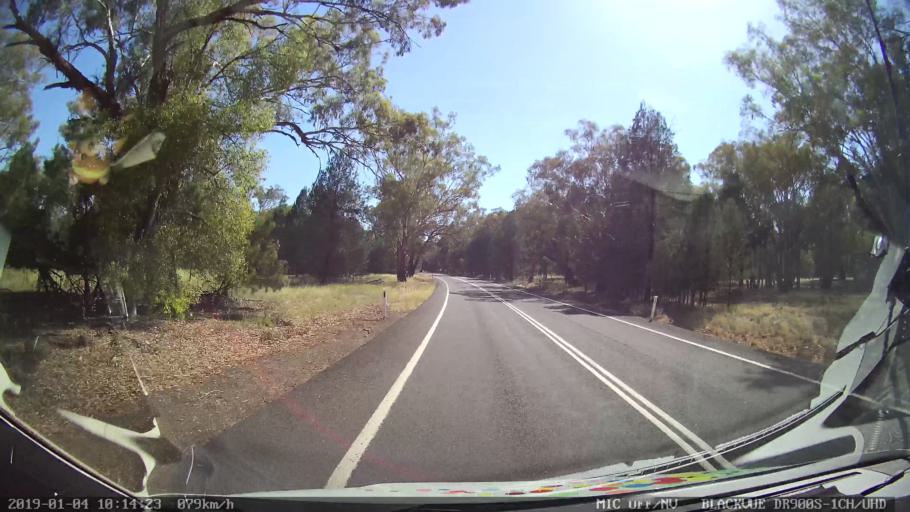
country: AU
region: New South Wales
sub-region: Cabonne
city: Canowindra
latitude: -33.3974
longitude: 148.4129
